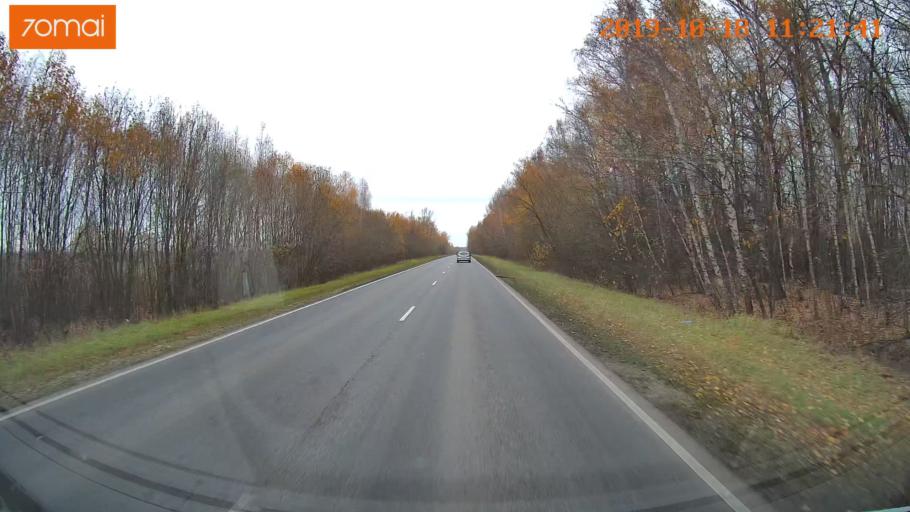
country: RU
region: Tula
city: Kimovsk
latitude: 54.0772
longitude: 38.5687
